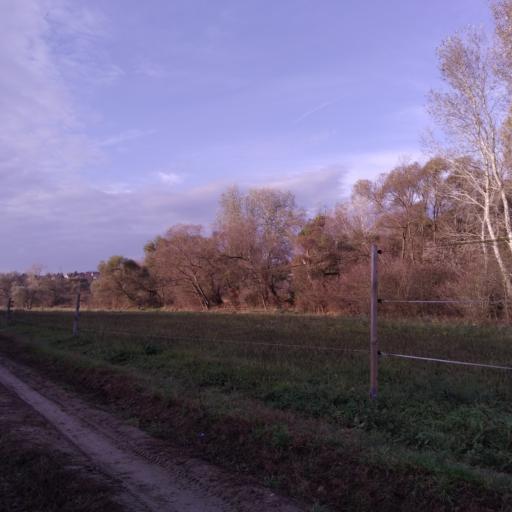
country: HU
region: Pest
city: Pomaz
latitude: 47.6270
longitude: 19.0272
